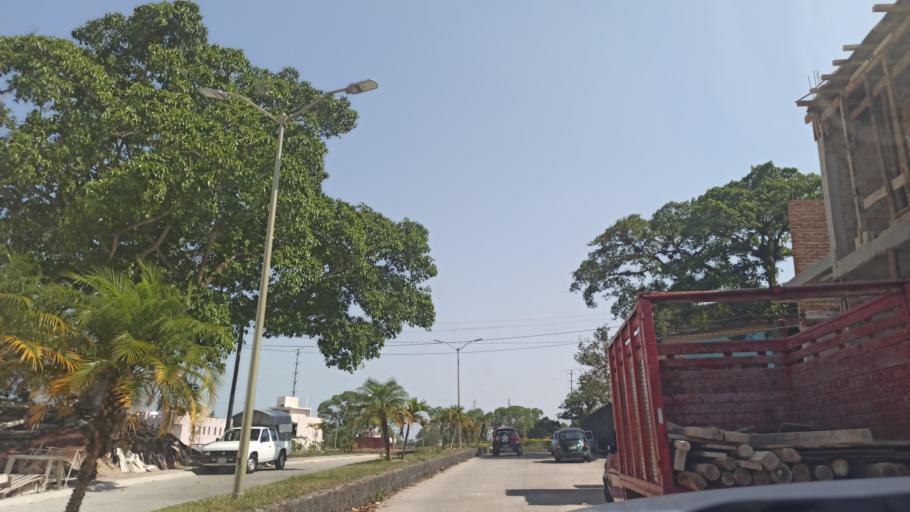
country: MX
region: Veracruz
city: El Castillo
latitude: 19.5284
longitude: -96.8656
